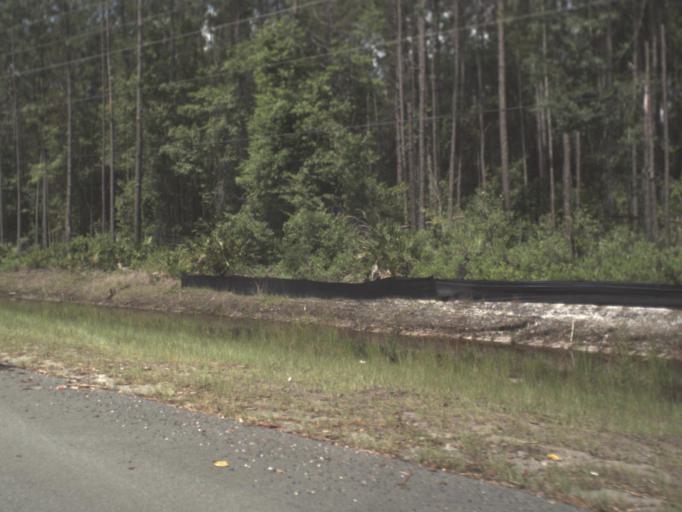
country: US
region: Florida
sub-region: Duval County
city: Baldwin
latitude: 30.4249
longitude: -81.9257
